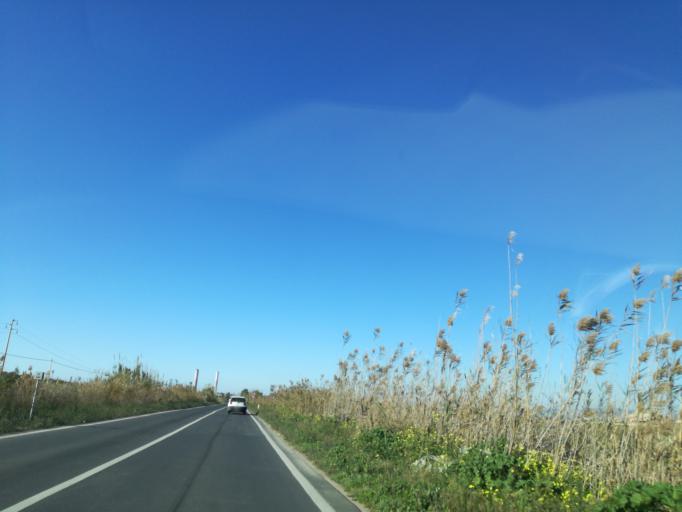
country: IT
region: Sicily
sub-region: Provincia di Caltanissetta
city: Gela
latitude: 37.0530
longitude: 14.3072
